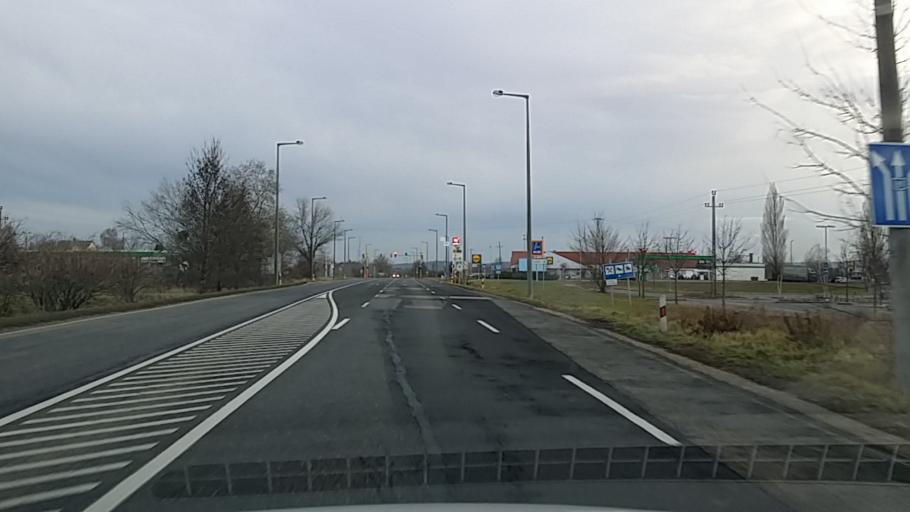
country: HU
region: Fejer
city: Mor
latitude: 47.3779
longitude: 18.1896
